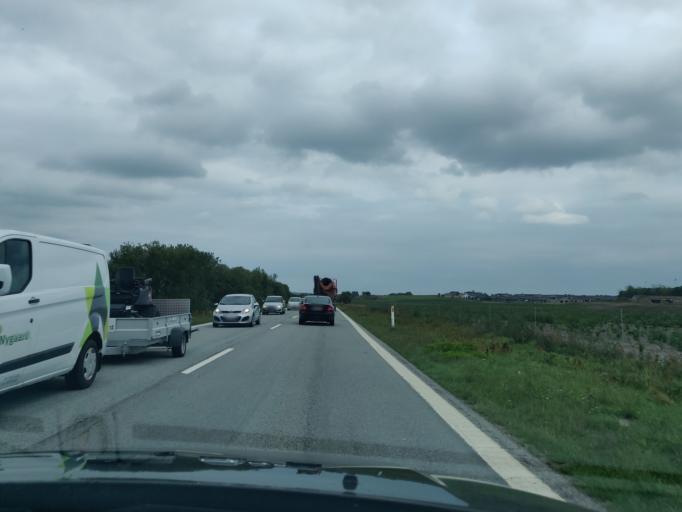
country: DK
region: North Denmark
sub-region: Alborg Kommune
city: Frejlev
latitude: 57.0125
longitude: 9.8002
